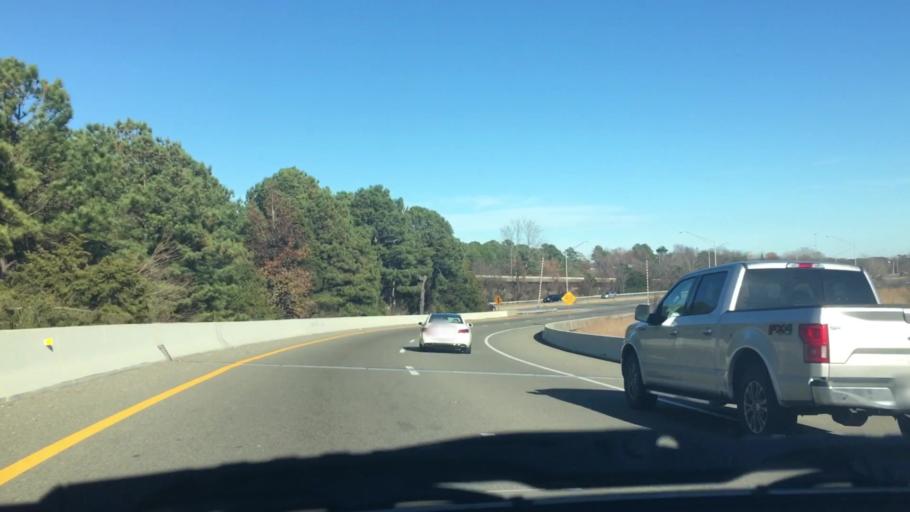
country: US
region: Virginia
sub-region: City of Hampton
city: Hampton
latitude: 37.0309
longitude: -76.3767
